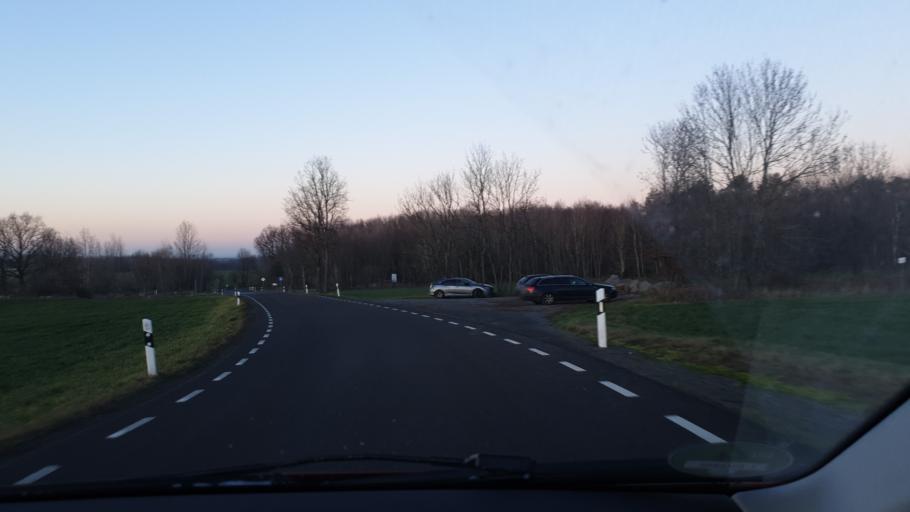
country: DE
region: Saxony
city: Hohburg
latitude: 51.4302
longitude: 12.7822
